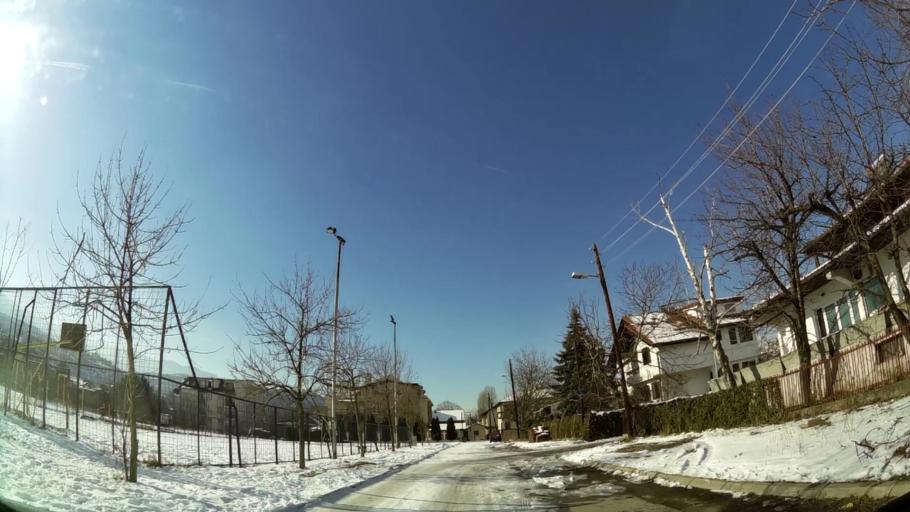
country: MK
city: Krushopek
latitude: 42.0009
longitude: 21.3716
